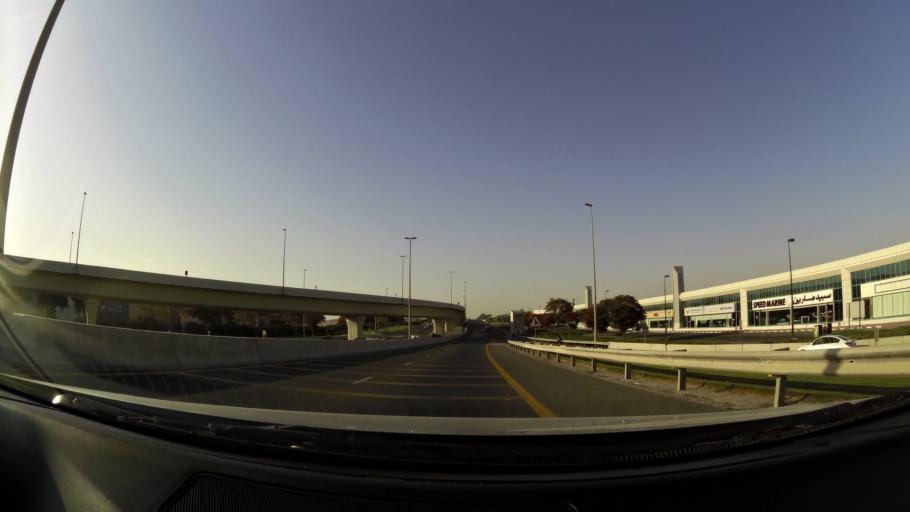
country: AE
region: Ash Shariqah
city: Sharjah
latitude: 25.1863
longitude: 55.3712
